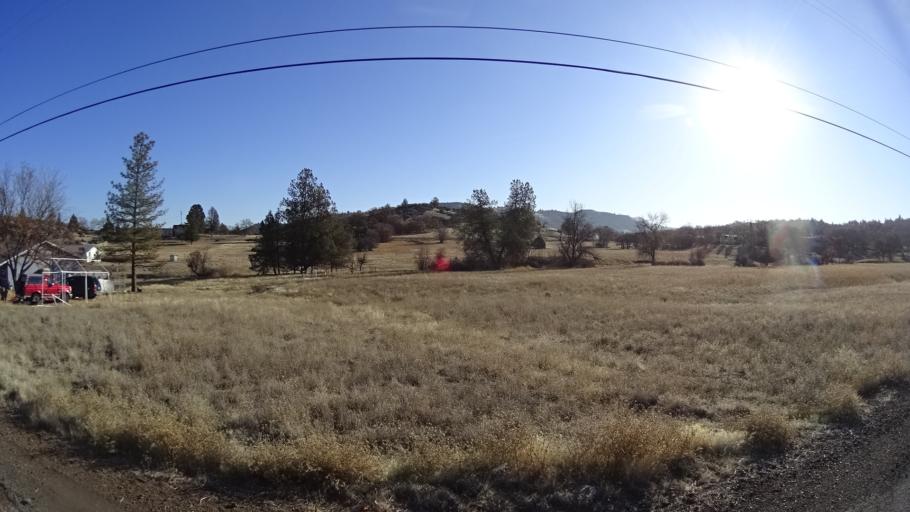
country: US
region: California
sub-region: Siskiyou County
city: Montague
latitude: 41.8896
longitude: -122.4916
